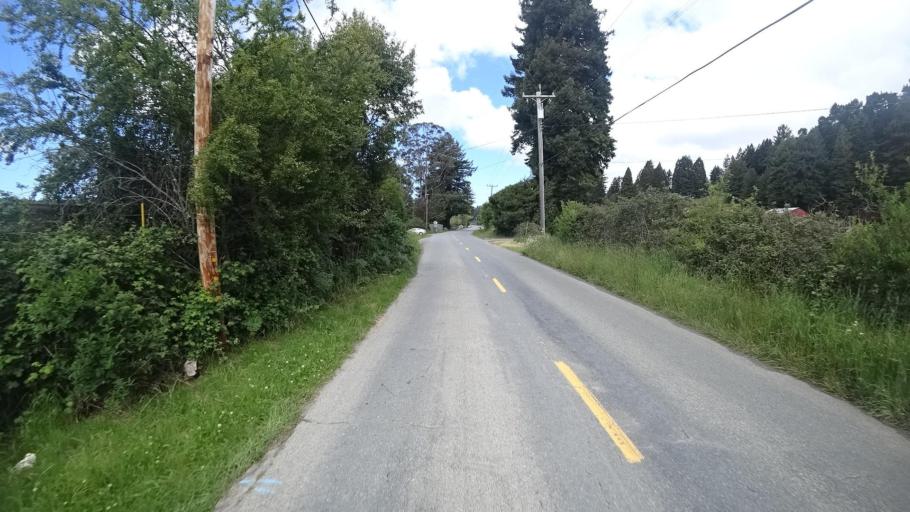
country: US
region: California
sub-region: Humboldt County
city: Blue Lake
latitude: 40.8933
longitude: -124.0031
